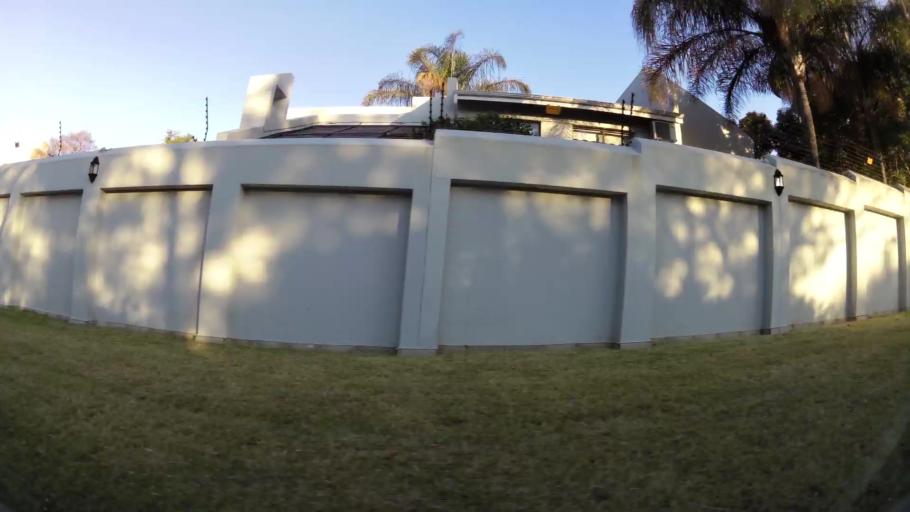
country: ZA
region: Gauteng
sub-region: City of Johannesburg Metropolitan Municipality
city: Midrand
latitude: -26.0712
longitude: 28.0590
